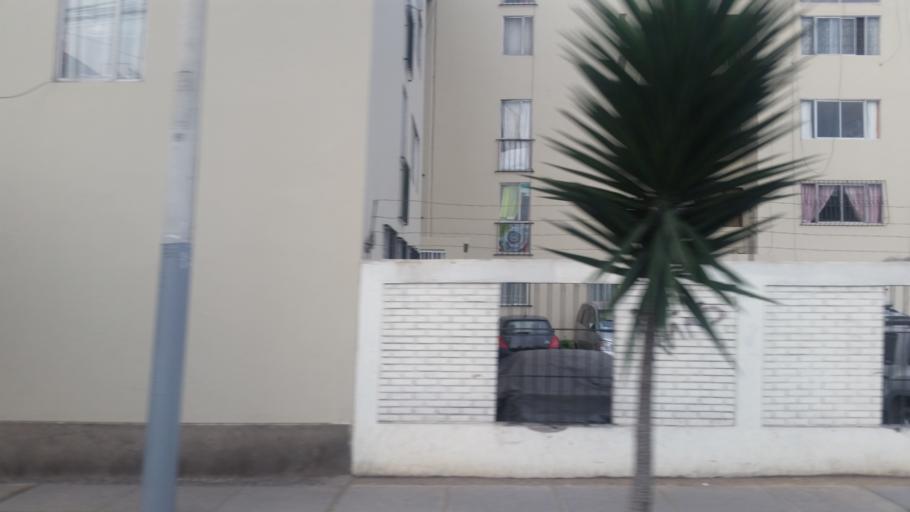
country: PE
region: Lima
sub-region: Lima
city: San Isidro
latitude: -12.0888
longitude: -77.0802
